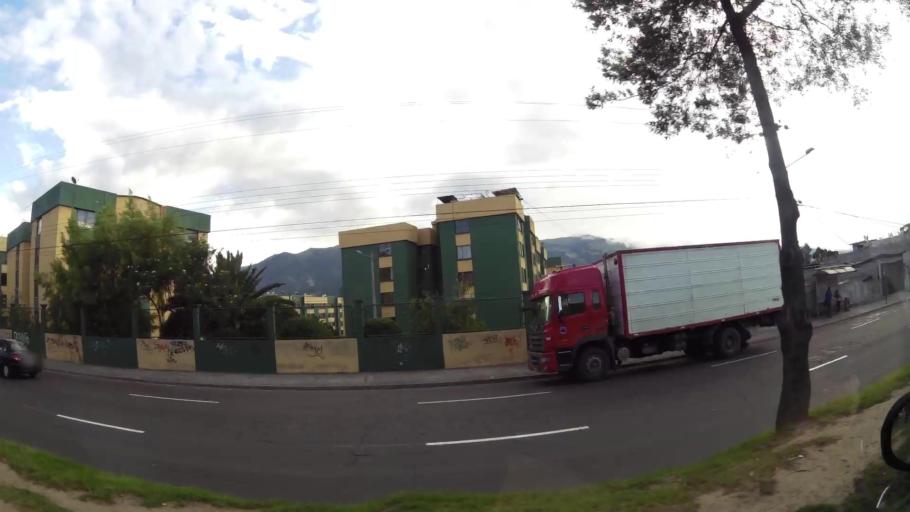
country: EC
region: Pichincha
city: Quito
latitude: -0.1298
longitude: -78.4755
